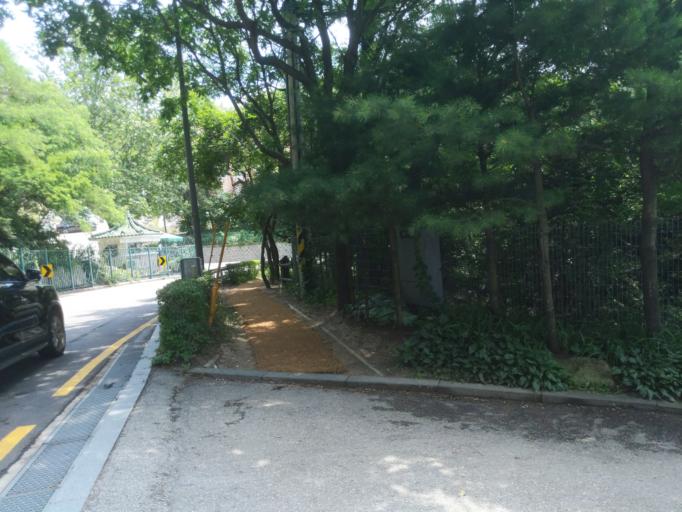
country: KR
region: Seoul
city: Seoul
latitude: 37.5980
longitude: 126.9741
